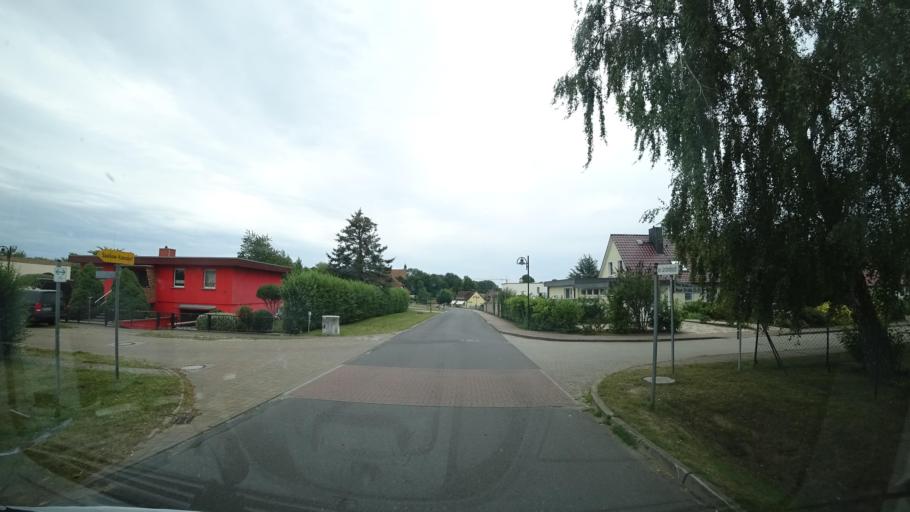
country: DE
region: Mecklenburg-Vorpommern
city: Rambin
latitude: 54.3064
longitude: 13.2116
